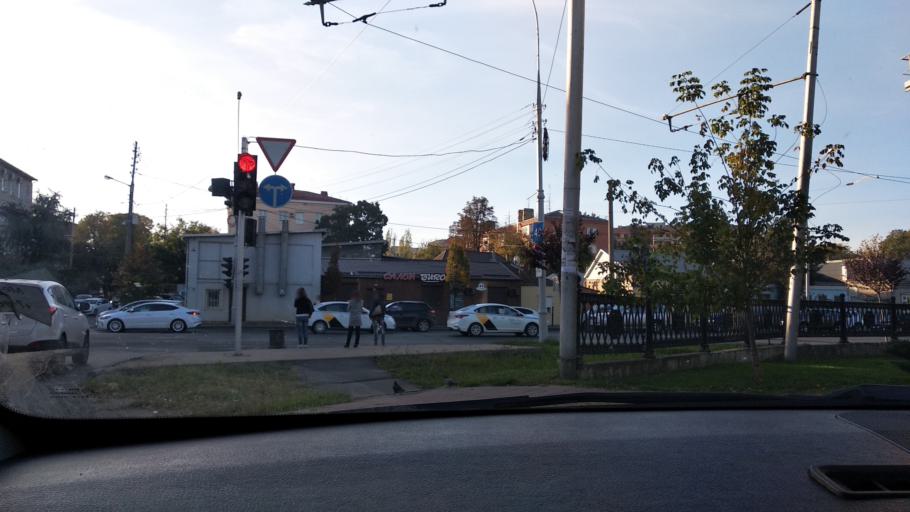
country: RU
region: Krasnodarskiy
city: Krasnodar
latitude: 45.0217
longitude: 38.9826
